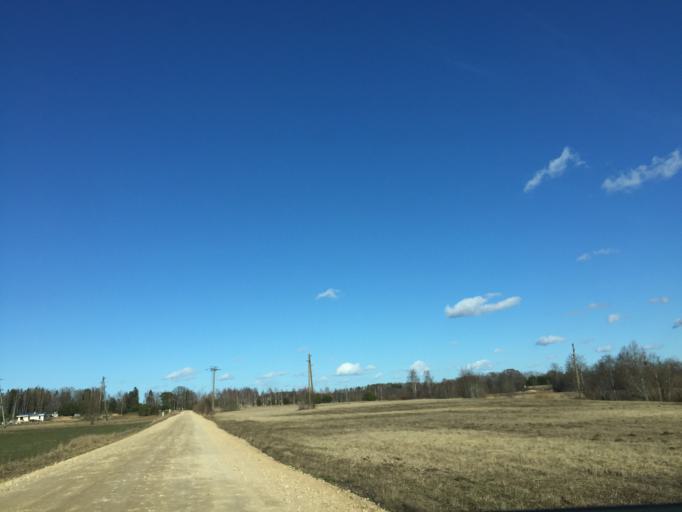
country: LV
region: Ogre
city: Ogre
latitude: 56.8596
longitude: 24.6969
